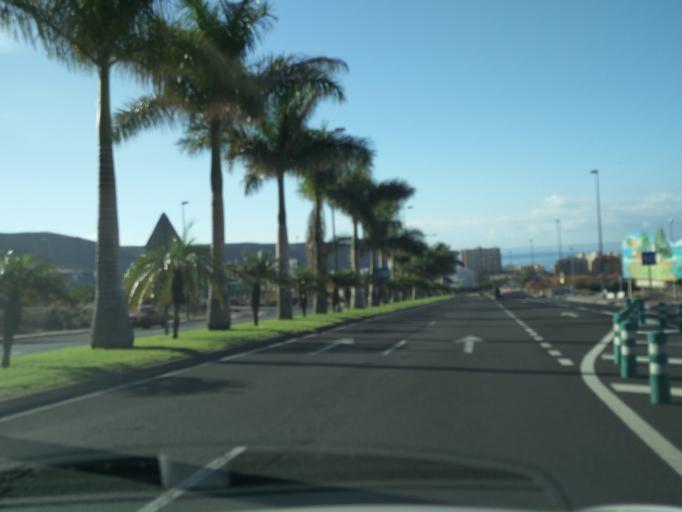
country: ES
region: Canary Islands
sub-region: Provincia de Santa Cruz de Tenerife
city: Playa de las Americas
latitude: 28.0626
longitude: -16.7111
